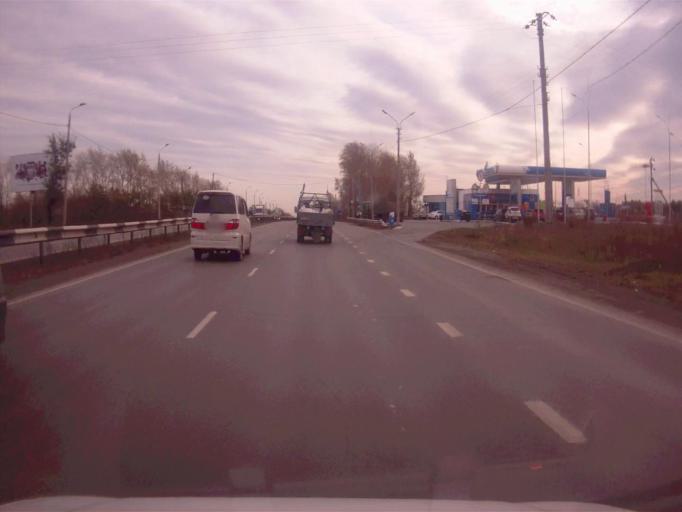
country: RU
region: Chelyabinsk
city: Novosineglazovskiy
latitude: 55.0558
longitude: 61.4070
